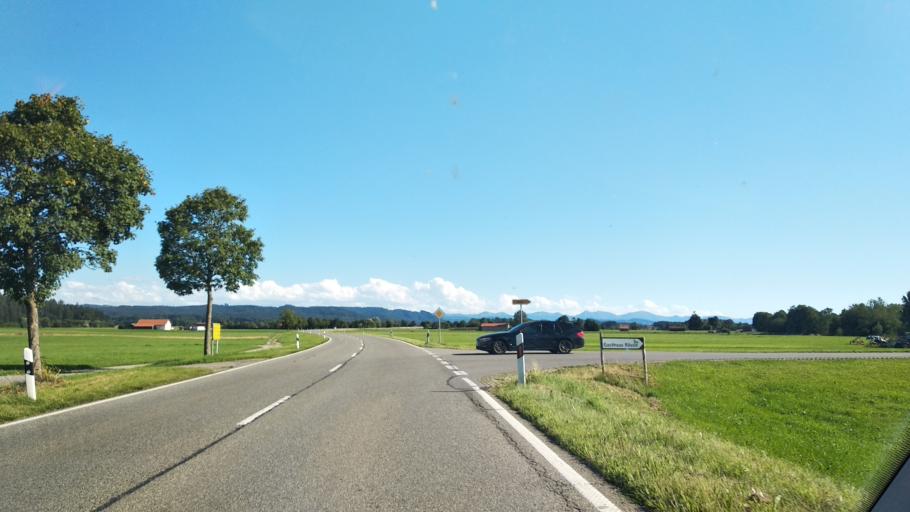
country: DE
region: Baden-Wuerttemberg
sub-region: Tuebingen Region
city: Leutkirch im Allgau
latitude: 47.7830
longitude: 10.0448
